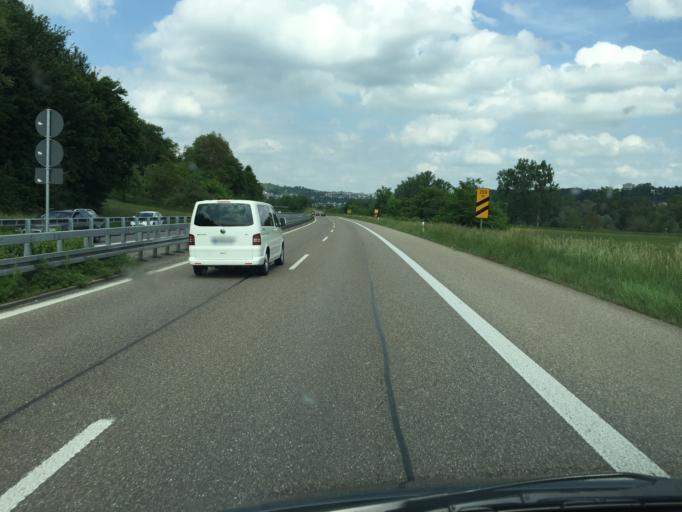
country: DE
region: Baden-Wuerttemberg
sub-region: Regierungsbezirk Stuttgart
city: Wernau
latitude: 48.6938
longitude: 9.4005
